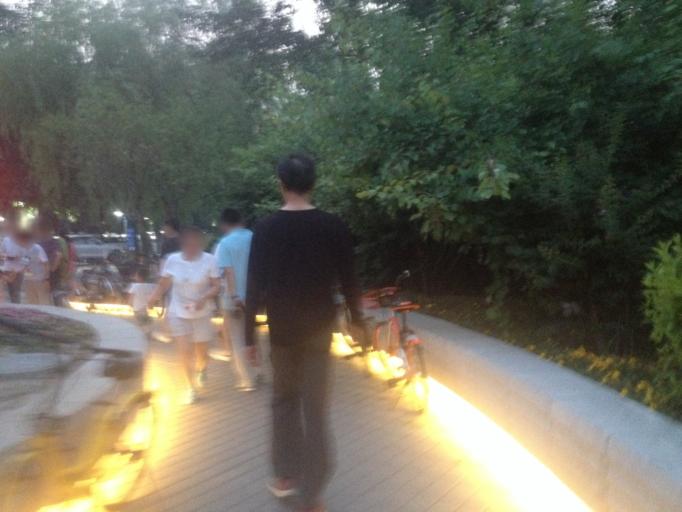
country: CN
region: Beijing
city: Datun
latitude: 40.0085
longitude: 116.3907
